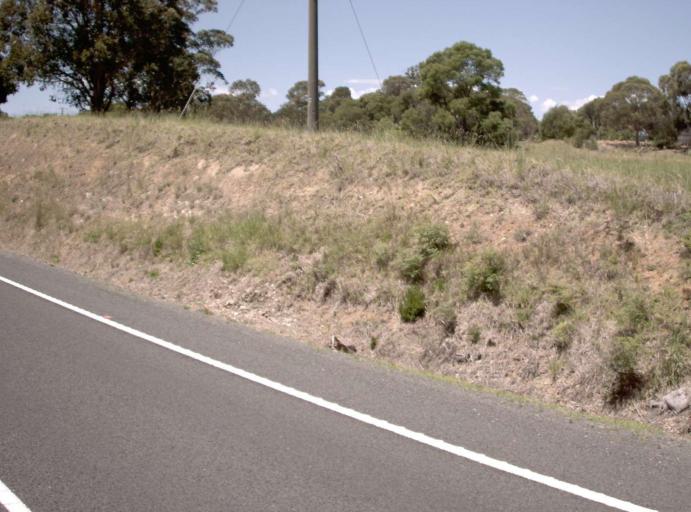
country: AU
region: Victoria
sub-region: East Gippsland
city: Lakes Entrance
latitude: -37.6996
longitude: 148.7183
